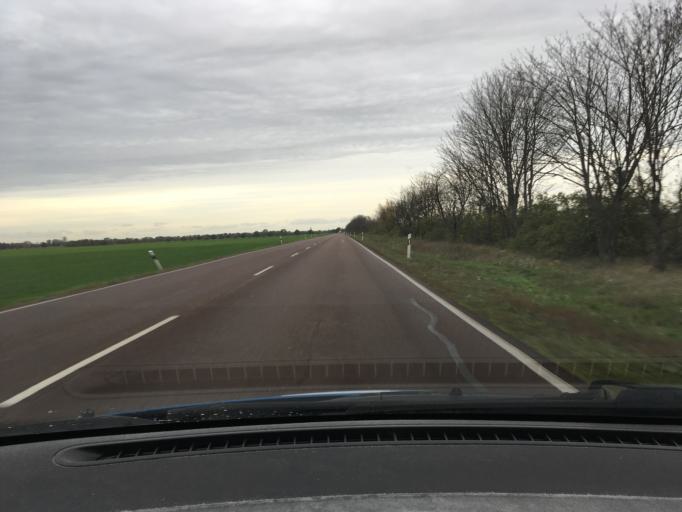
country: DE
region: Saxony-Anhalt
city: Zerbst
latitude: 51.9817
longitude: 12.0564
